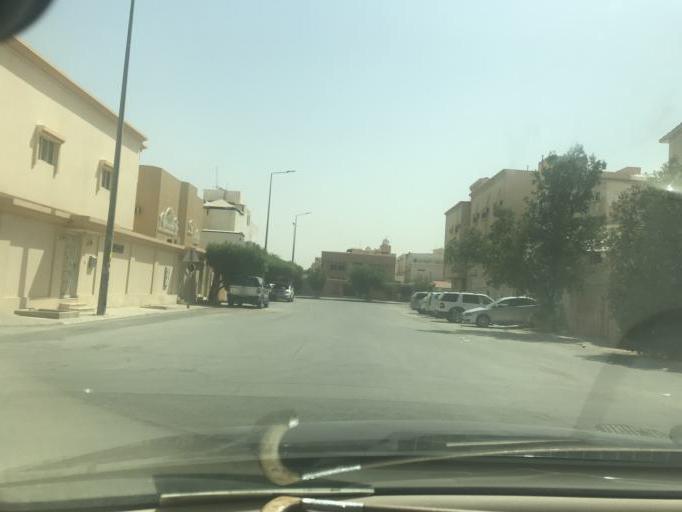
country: SA
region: Ar Riyad
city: Riyadh
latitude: 24.7455
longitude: 46.7650
